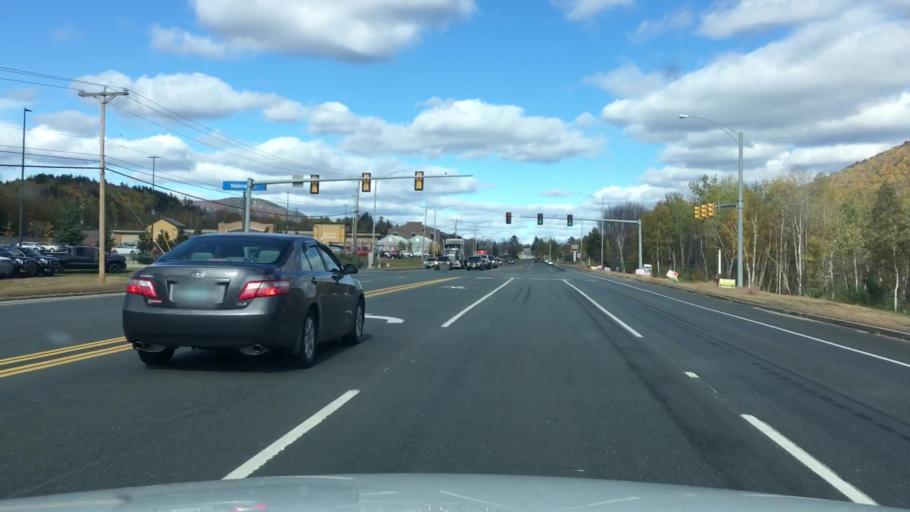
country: US
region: New Hampshire
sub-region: Coos County
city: Gorham
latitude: 44.4235
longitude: -71.1938
